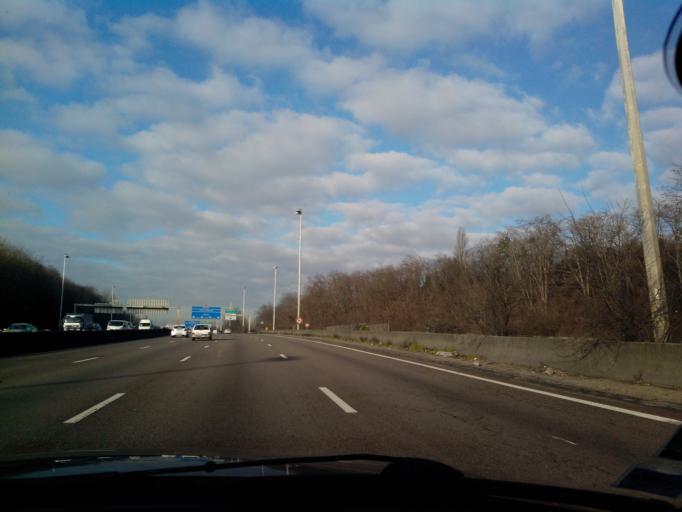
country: FR
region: Ile-de-France
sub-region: Departement du Val-d'Oise
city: Saint-Gratien
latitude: 48.9582
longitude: 2.2751
